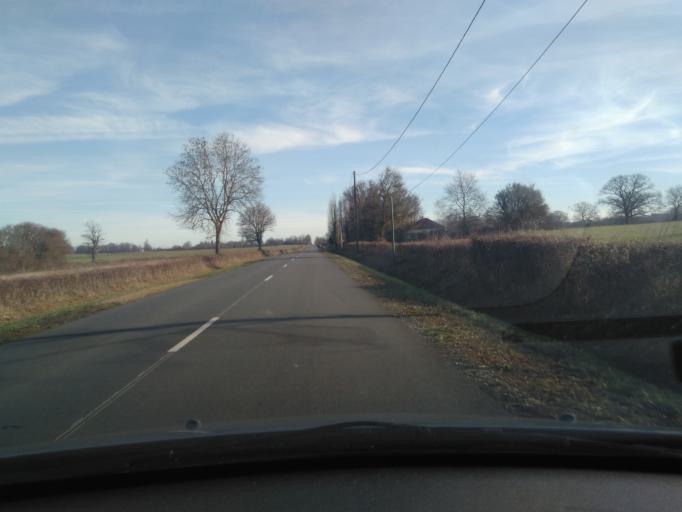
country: FR
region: Centre
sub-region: Departement du Cher
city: Orval
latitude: 46.6532
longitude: 2.3917
